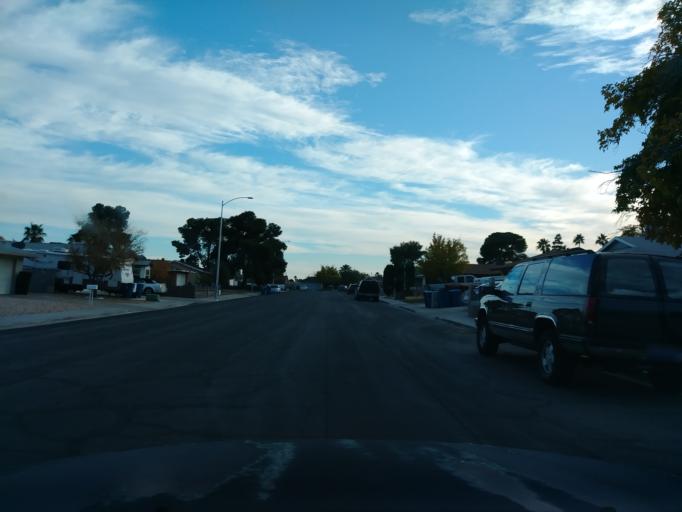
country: US
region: Nevada
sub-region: Clark County
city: Spring Valley
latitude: 36.1686
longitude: -115.2413
